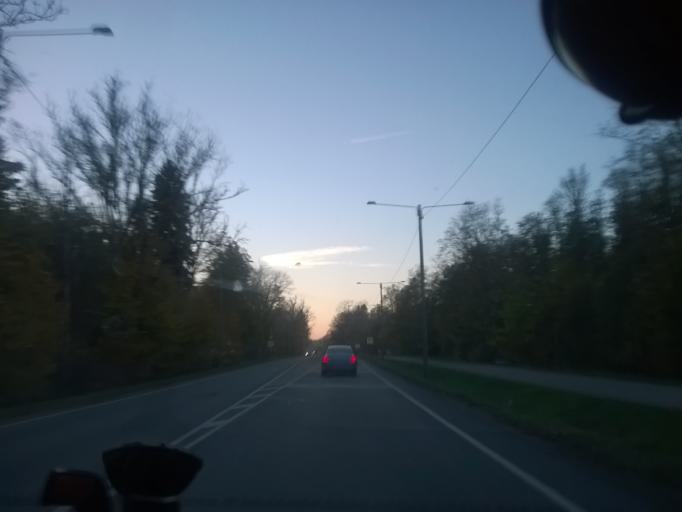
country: EE
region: Laeaene
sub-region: Ridala Parish
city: Uuemoisa
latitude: 58.9562
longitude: 23.7503
